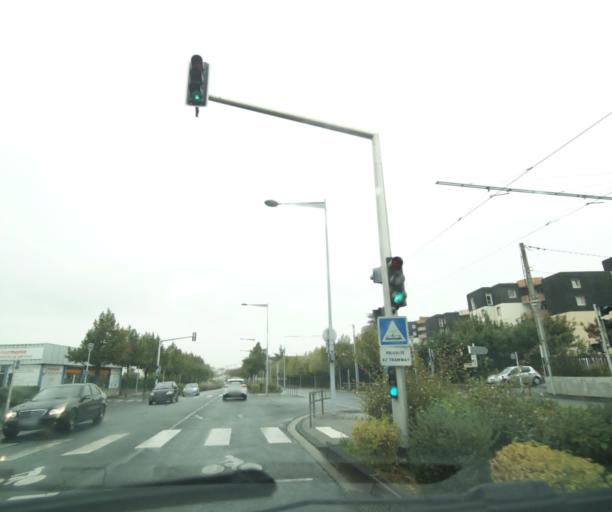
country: FR
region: Auvergne
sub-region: Departement du Puy-de-Dome
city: Cebazat
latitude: 45.8061
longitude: 3.1068
